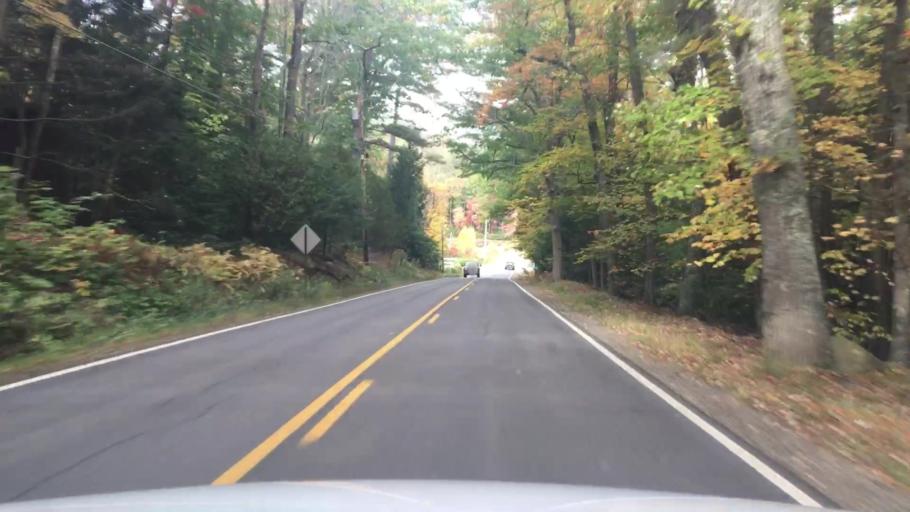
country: US
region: Maine
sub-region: Knox County
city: Camden
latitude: 44.2331
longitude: -69.1063
